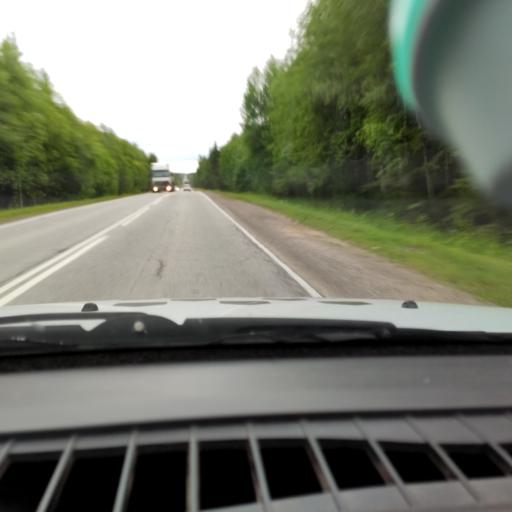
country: RU
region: Perm
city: Lys'va
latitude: 58.1243
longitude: 57.7191
